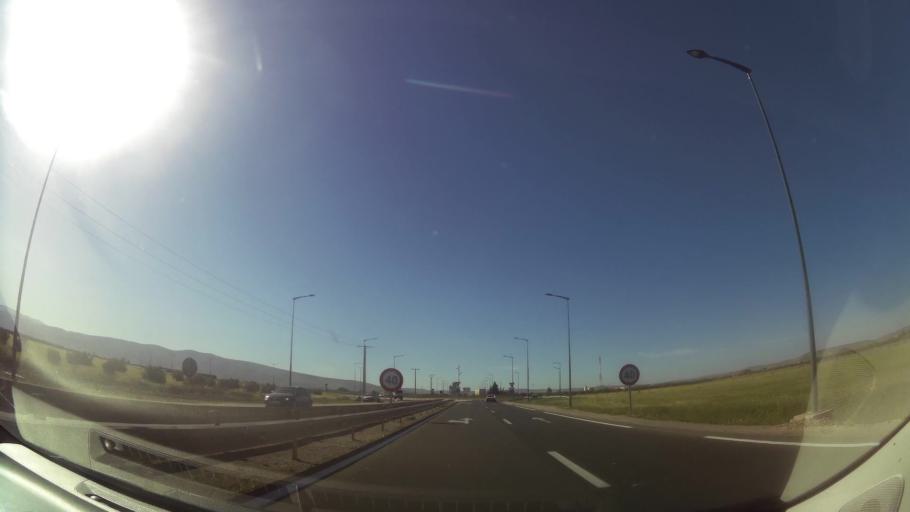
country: MA
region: Oriental
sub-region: Berkane-Taourirt
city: Ahfir
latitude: 34.8393
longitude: -1.9803
